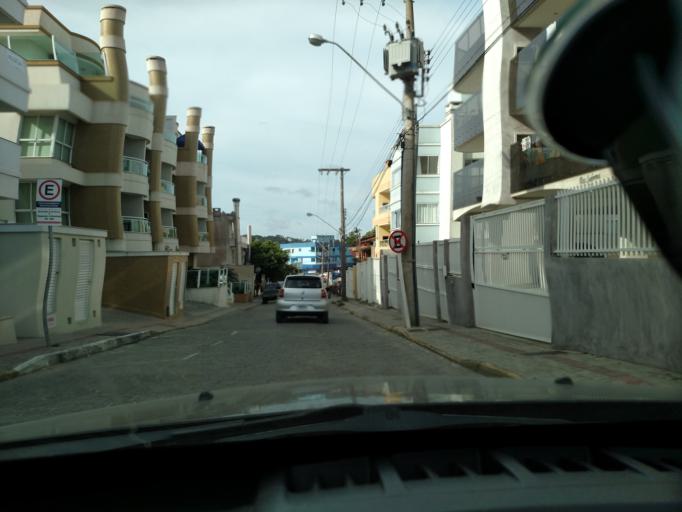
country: BR
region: Santa Catarina
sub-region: Porto Belo
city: Porto Belo
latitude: -27.1498
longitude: -48.4846
